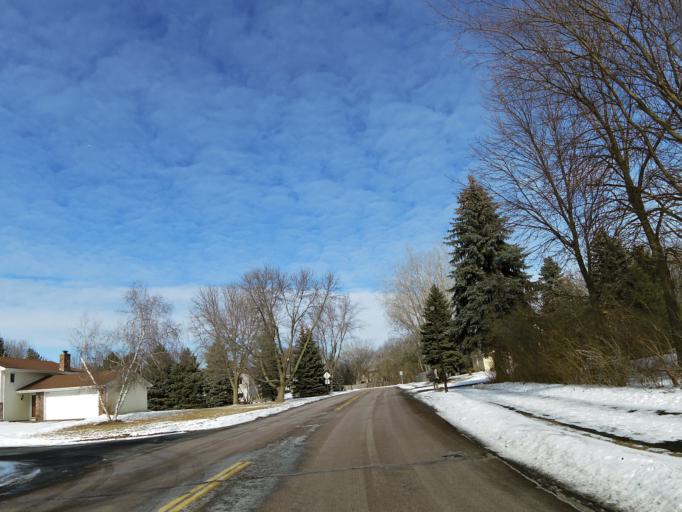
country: US
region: Minnesota
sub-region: Hennepin County
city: Eden Prairie
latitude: 44.8138
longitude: -93.4198
